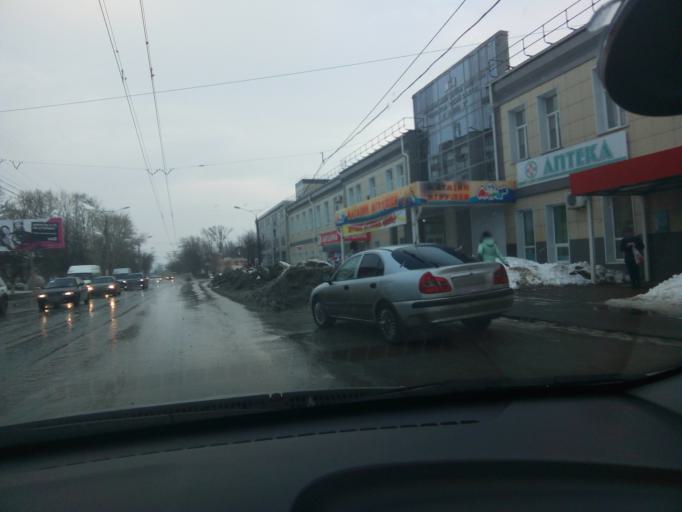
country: RU
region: Chuvashia
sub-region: Cheboksarskiy Rayon
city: Cheboksary
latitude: 56.1249
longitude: 47.2065
